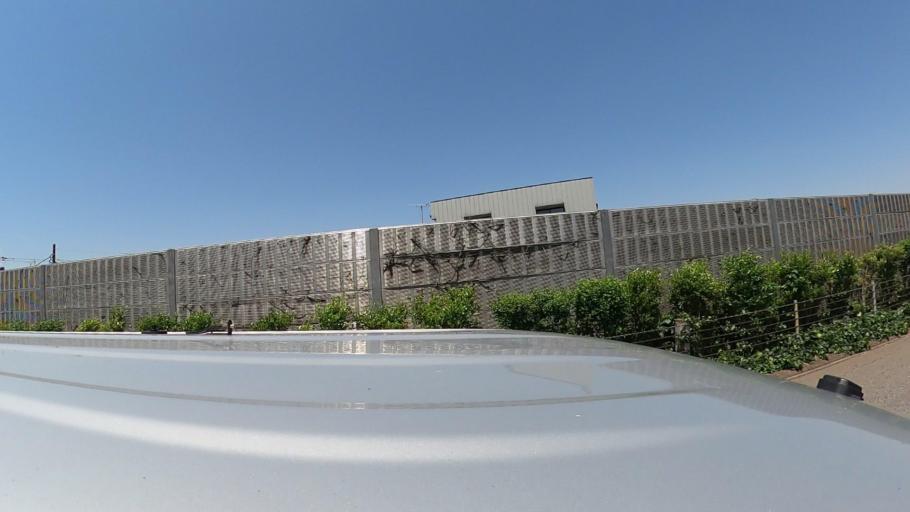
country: JP
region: Ibaraki
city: Mitsukaido
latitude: 36.0083
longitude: 140.0454
